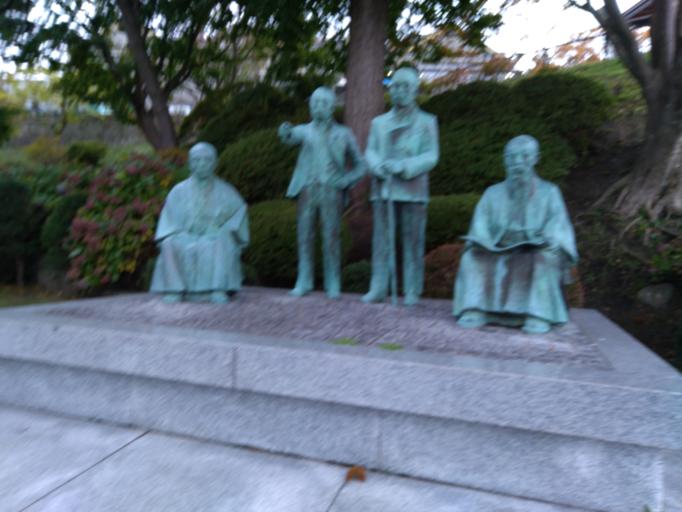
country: JP
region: Hokkaido
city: Hakodate
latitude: 41.7656
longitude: 140.7093
